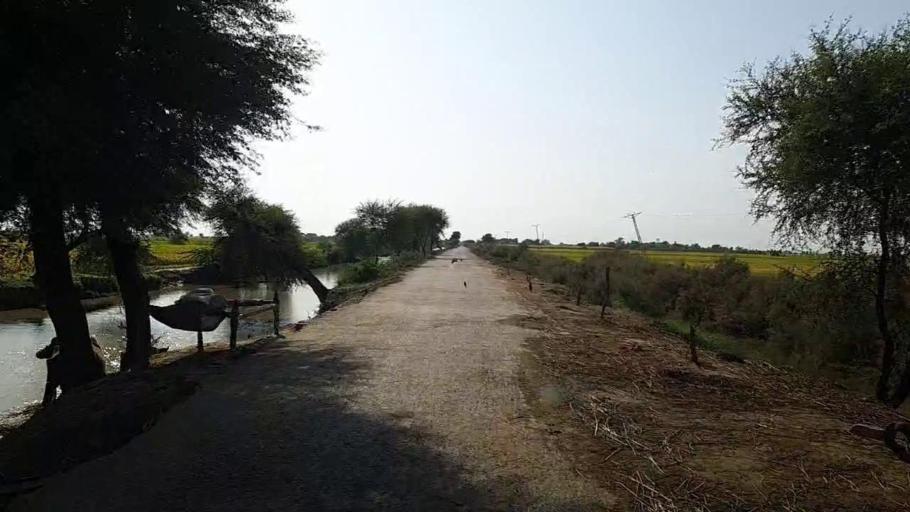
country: PK
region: Sindh
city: Kario
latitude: 24.8064
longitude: 68.5406
